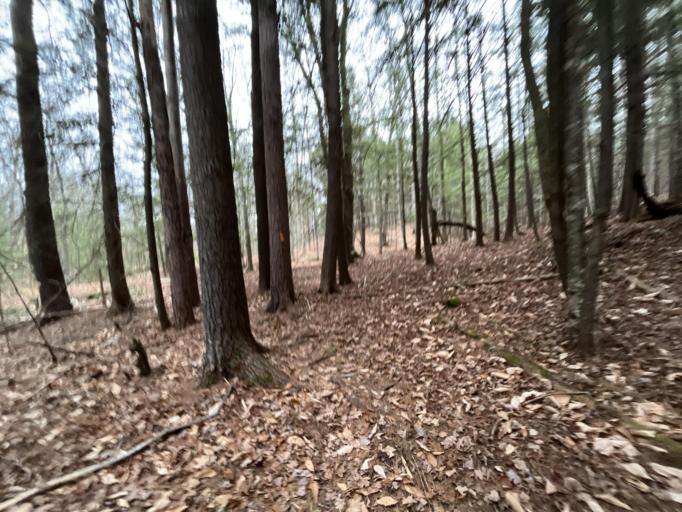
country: US
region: New Hampshire
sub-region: Merrimack County
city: New London
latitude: 43.4033
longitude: -71.9794
